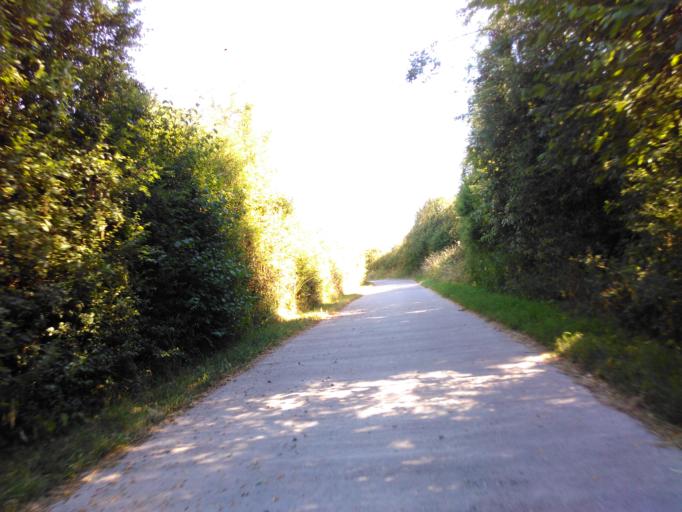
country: LU
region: Luxembourg
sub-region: Canton d'Esch-sur-Alzette
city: Sanem
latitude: 49.5406
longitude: 5.9223
